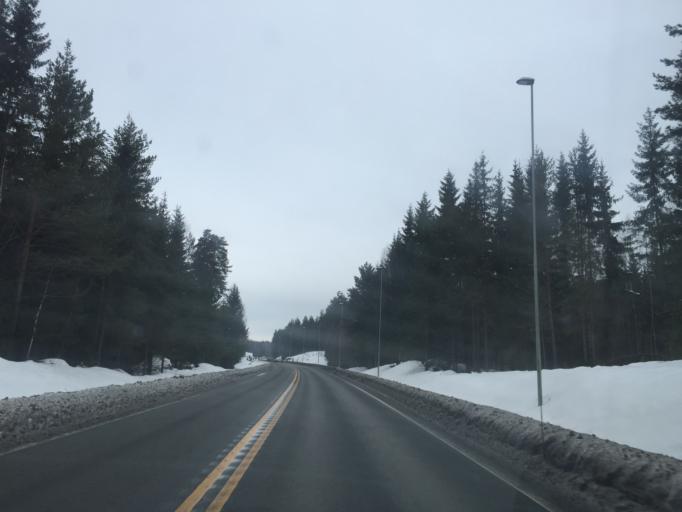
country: NO
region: Hedmark
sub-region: Stange
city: Stange
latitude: 60.7227
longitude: 11.2906
